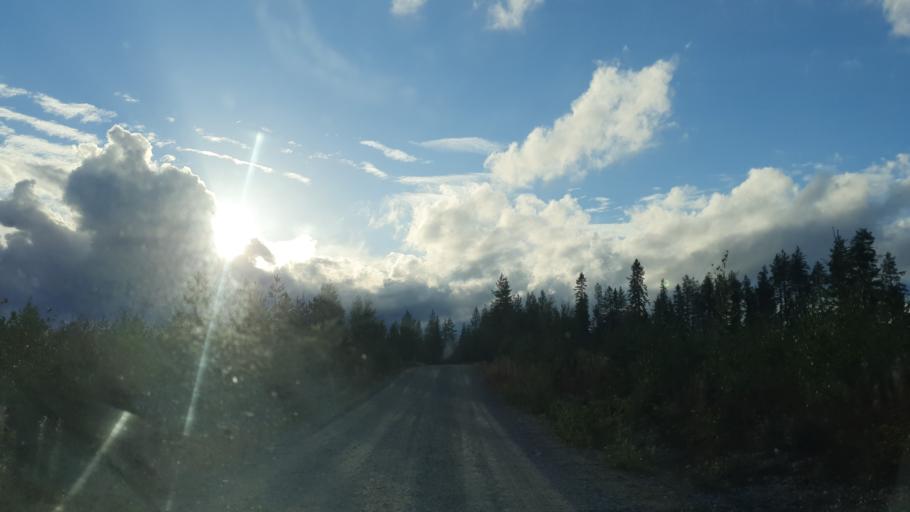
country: FI
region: Kainuu
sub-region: Kehys-Kainuu
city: Kuhmo
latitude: 64.3365
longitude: 29.9567
